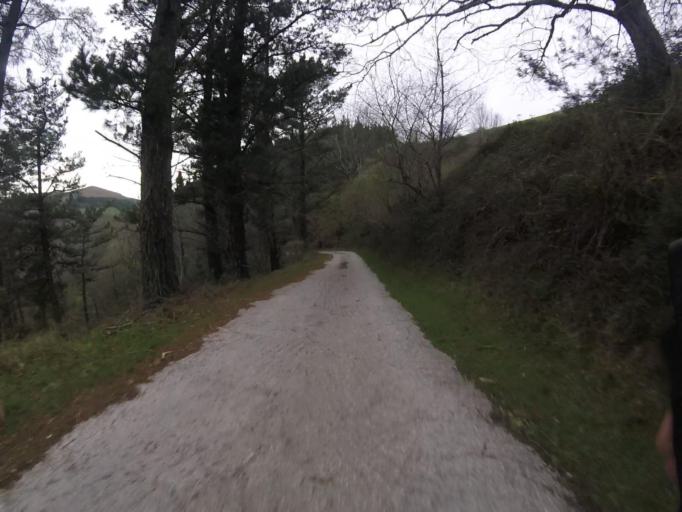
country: ES
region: Navarre
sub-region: Provincia de Navarra
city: Lesaka
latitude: 43.2796
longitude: -1.7470
